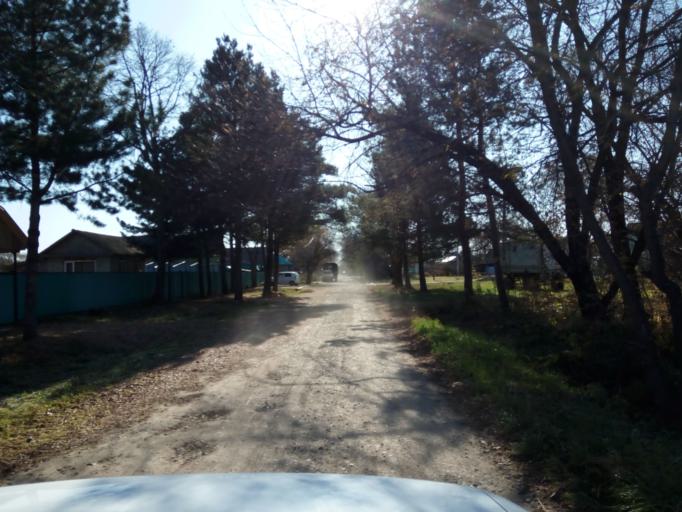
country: RU
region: Primorskiy
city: Dal'nerechensk
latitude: 45.9091
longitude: 133.7987
